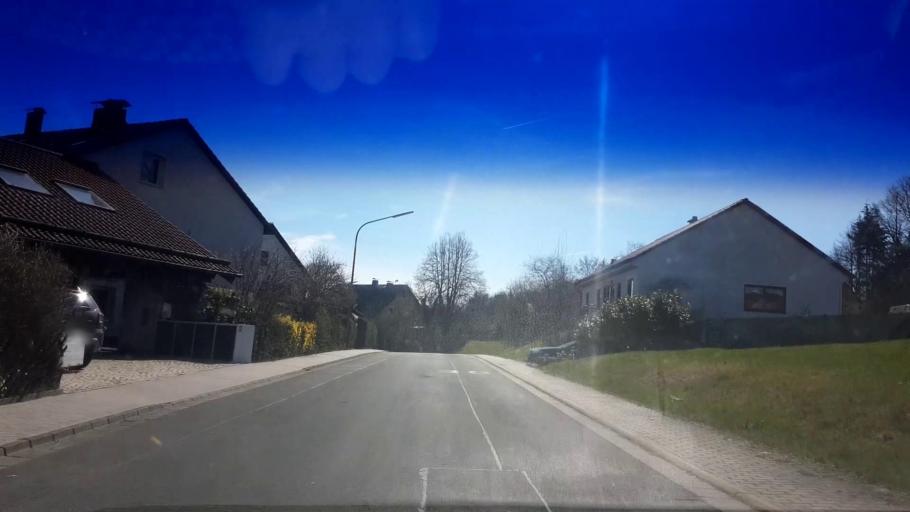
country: DE
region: Bavaria
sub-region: Upper Franconia
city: Bindlach
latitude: 50.0102
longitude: 11.6256
